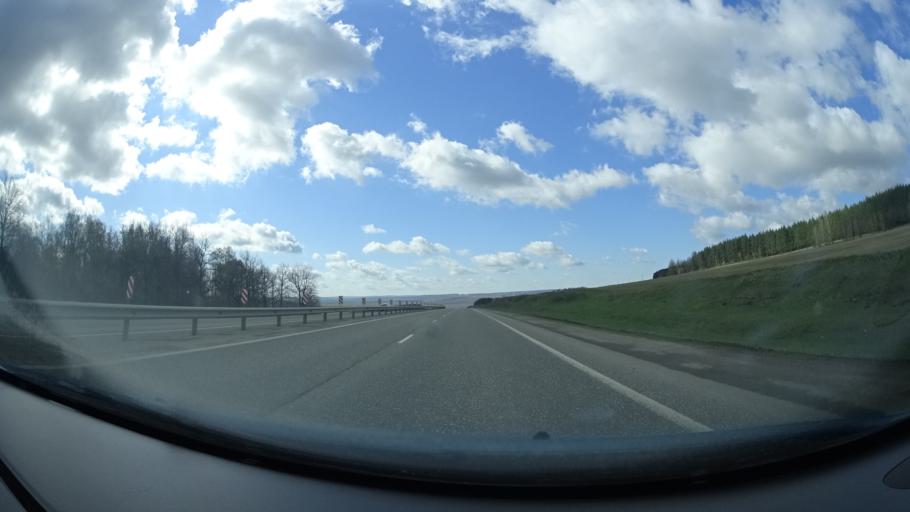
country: RU
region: Bashkortostan
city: Tolbazy
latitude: 54.1009
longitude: 55.8994
